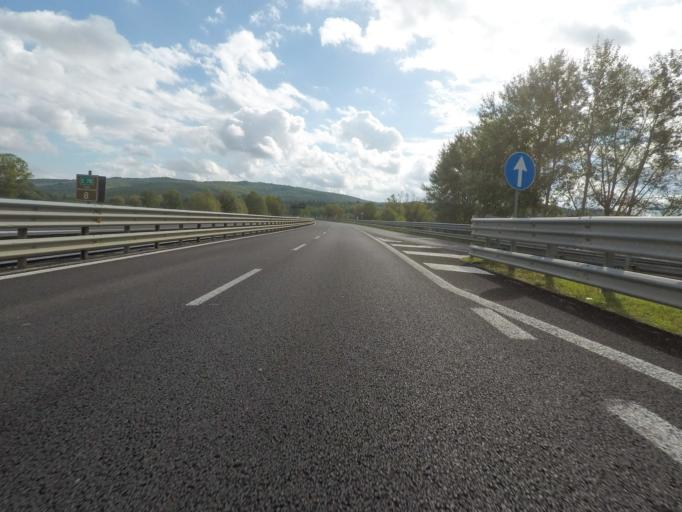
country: IT
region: Tuscany
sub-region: Provincia di Siena
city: Serre di Rapolano
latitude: 43.2483
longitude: 11.6449
